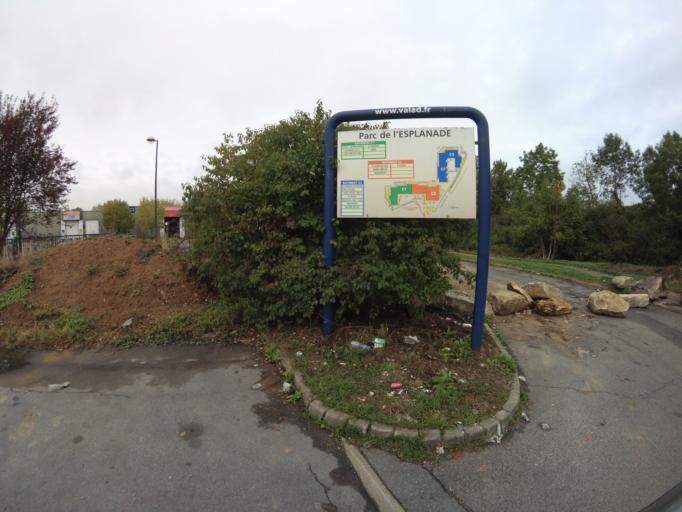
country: FR
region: Ile-de-France
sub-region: Departement de Seine-et-Marne
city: Saint-Thibault-des-Vignes
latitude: 48.8662
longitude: 2.6762
